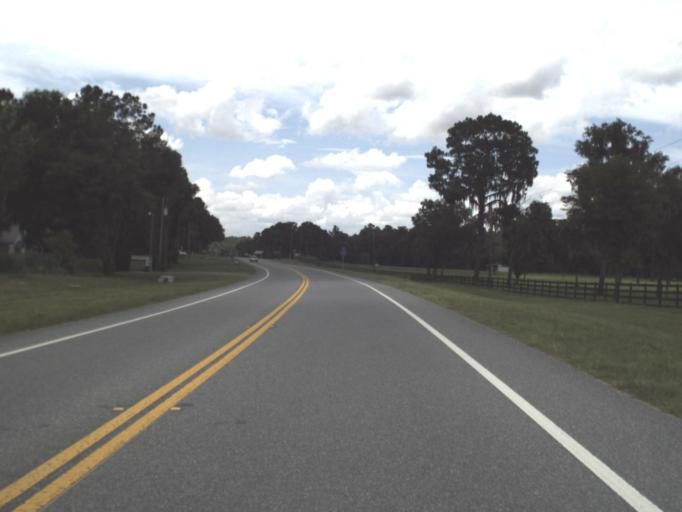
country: US
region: Florida
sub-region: Suwannee County
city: Live Oak
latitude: 30.3814
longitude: -82.9380
